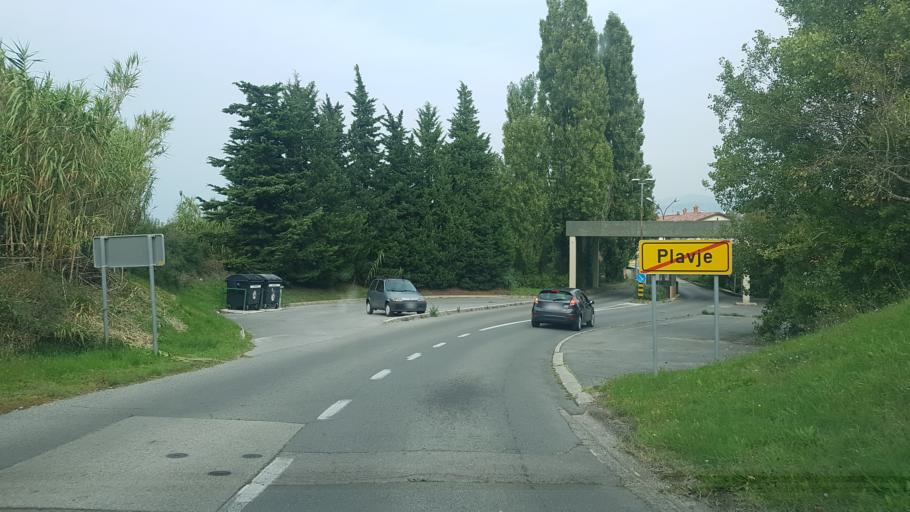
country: SI
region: Koper-Capodistria
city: Spodnje Skofije
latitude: 45.5809
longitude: 13.8031
